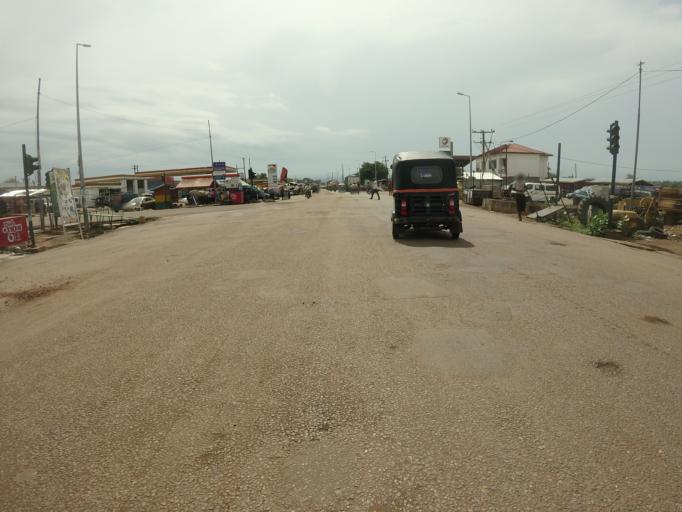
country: GH
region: Upper East
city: Bolgatanga
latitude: 10.7837
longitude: -0.8481
